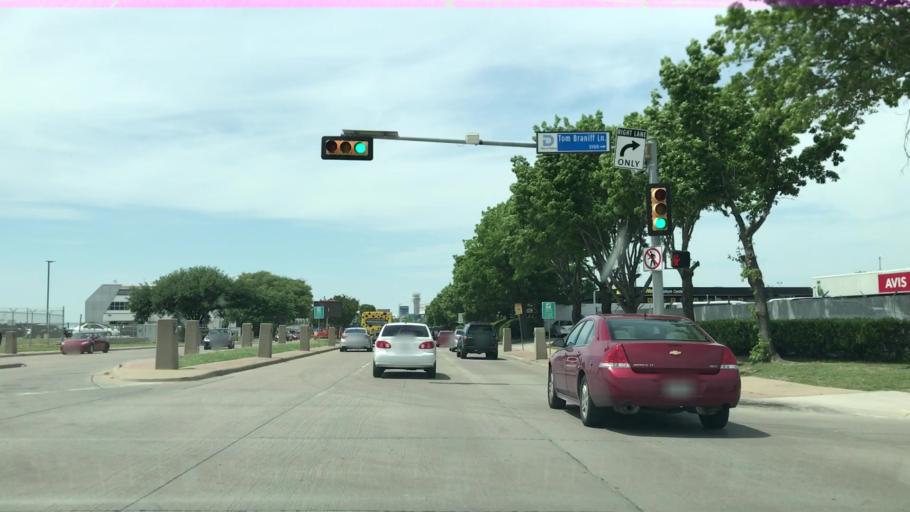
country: US
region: Texas
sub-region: Dallas County
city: University Park
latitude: 32.8365
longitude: -96.8425
